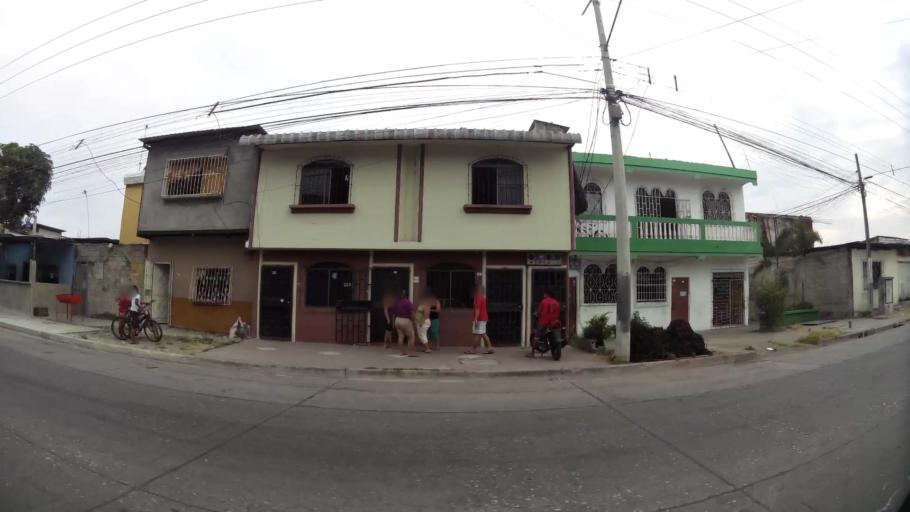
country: EC
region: Guayas
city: Guayaquil
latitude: -2.2544
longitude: -79.8740
